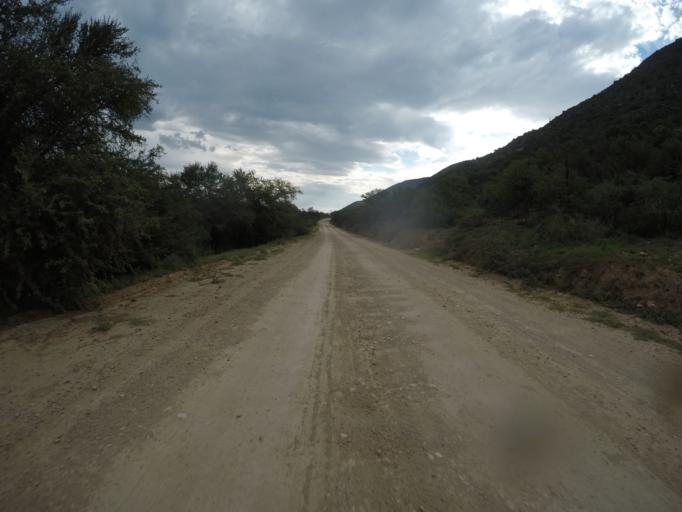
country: ZA
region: Eastern Cape
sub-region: Cacadu District Municipality
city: Kareedouw
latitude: -33.5734
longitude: 24.1345
